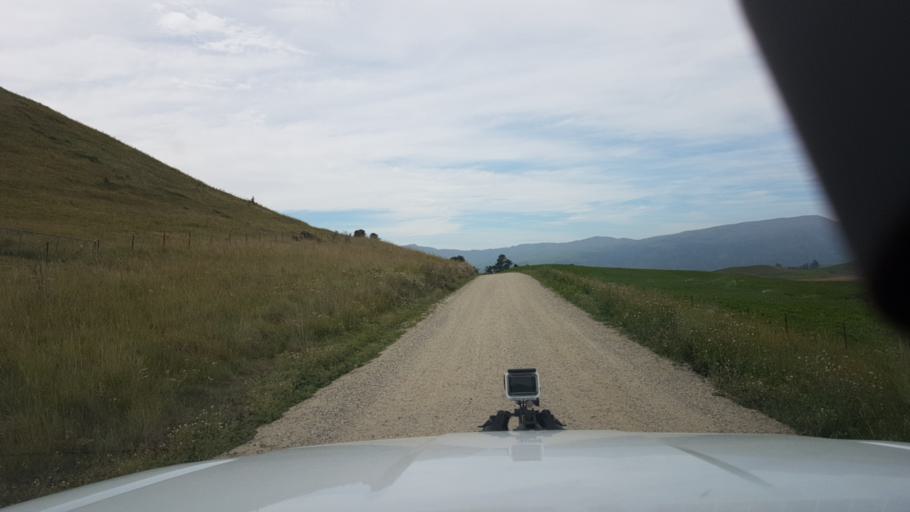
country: NZ
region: Otago
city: Oamaru
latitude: -44.8695
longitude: 170.6474
